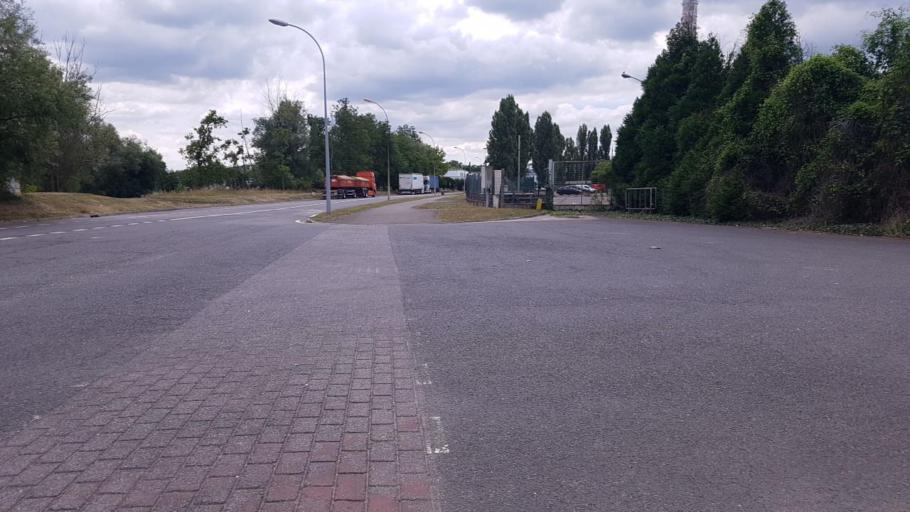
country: FR
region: Picardie
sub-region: Departement de l'Oise
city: Clairoix
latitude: 49.4323
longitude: 2.8582
